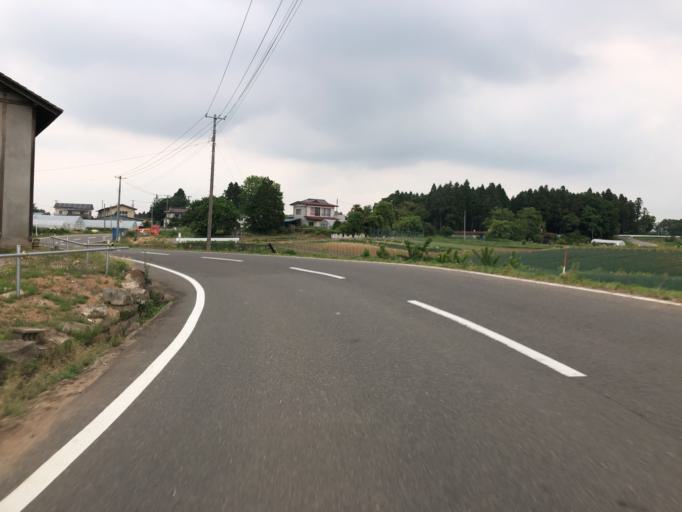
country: JP
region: Fukushima
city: Nihommatsu
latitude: 37.6391
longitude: 140.4796
